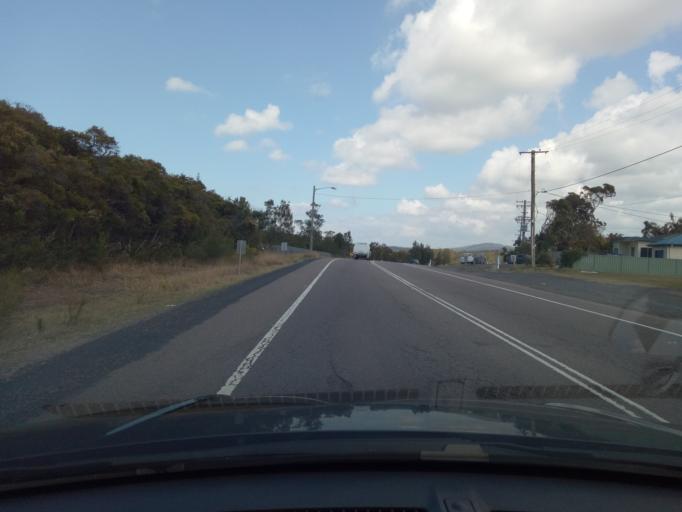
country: AU
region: New South Wales
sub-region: Gosford Shire
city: Forresters Beach
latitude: -33.4081
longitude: 151.4631
